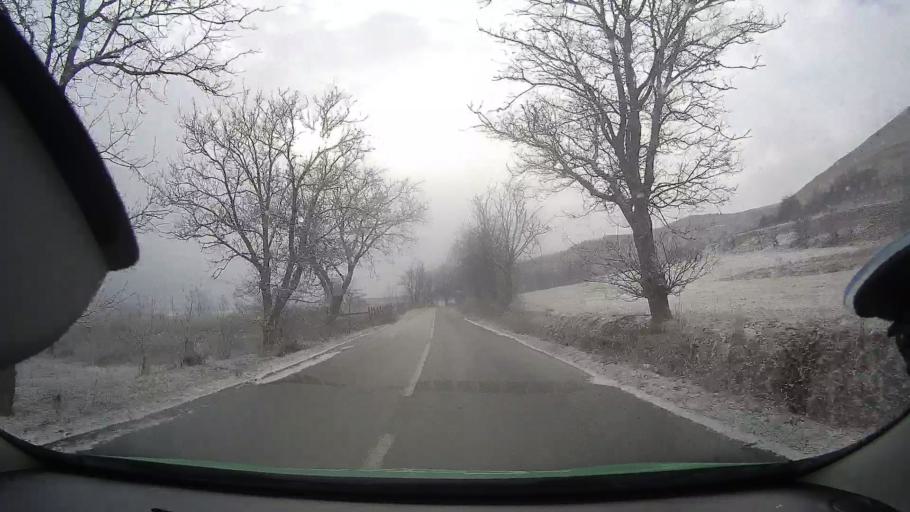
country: RO
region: Alba
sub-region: Comuna Rimetea
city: Rimetea
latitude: 46.4364
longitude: 23.5615
